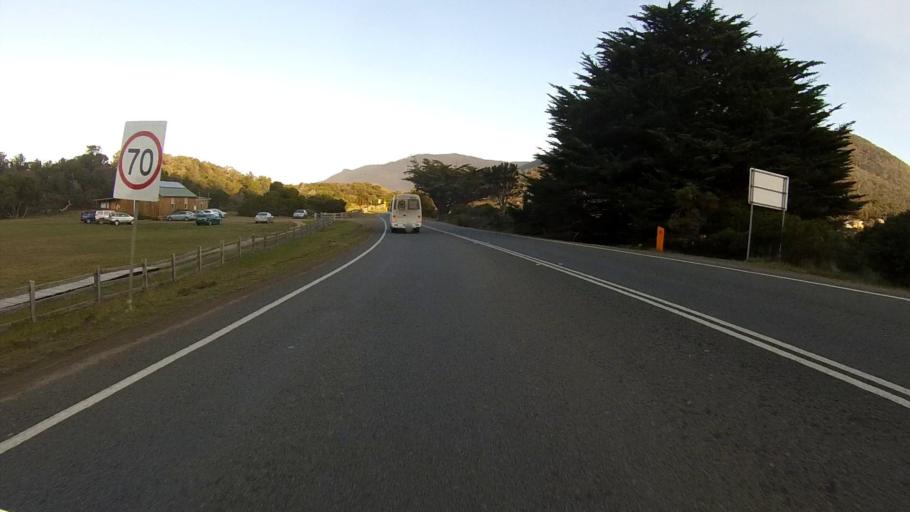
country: AU
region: Tasmania
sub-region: Sorell
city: Sorell
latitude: -43.0147
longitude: 147.9248
